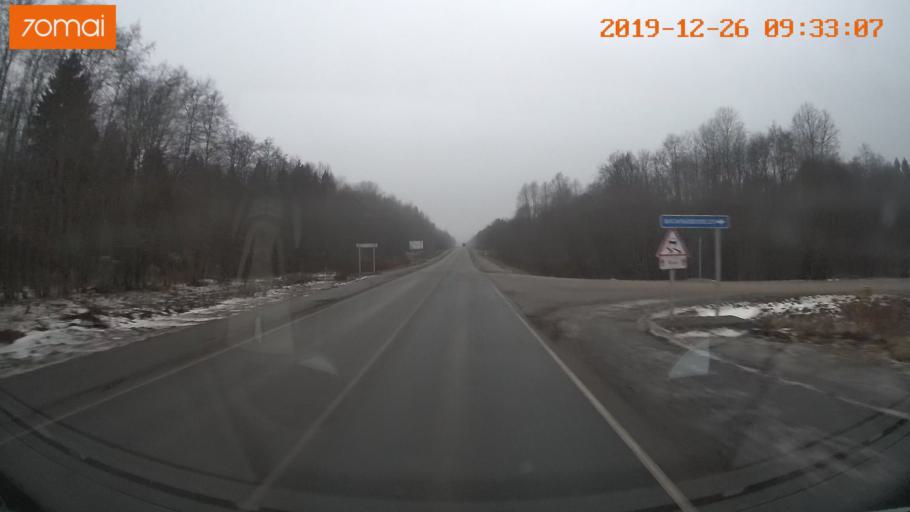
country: RU
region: Vologda
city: Gryazovets
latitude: 59.0860
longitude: 40.1057
